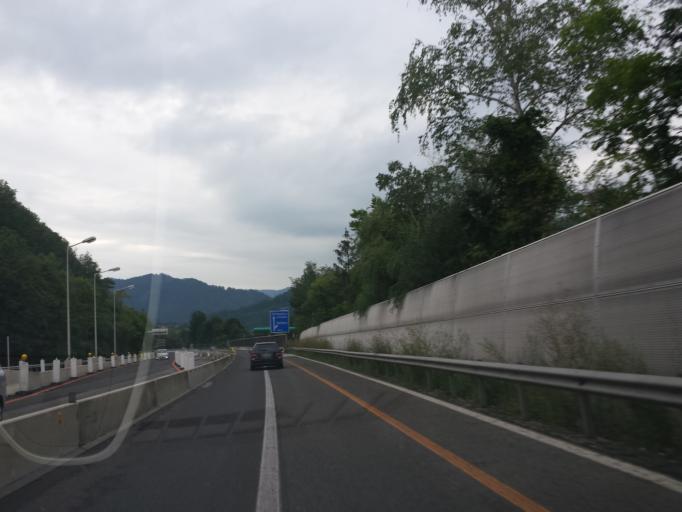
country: AT
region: Styria
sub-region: Politischer Bezirk Graz-Umgebung
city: Frohnleiten
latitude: 47.2742
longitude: 15.3280
